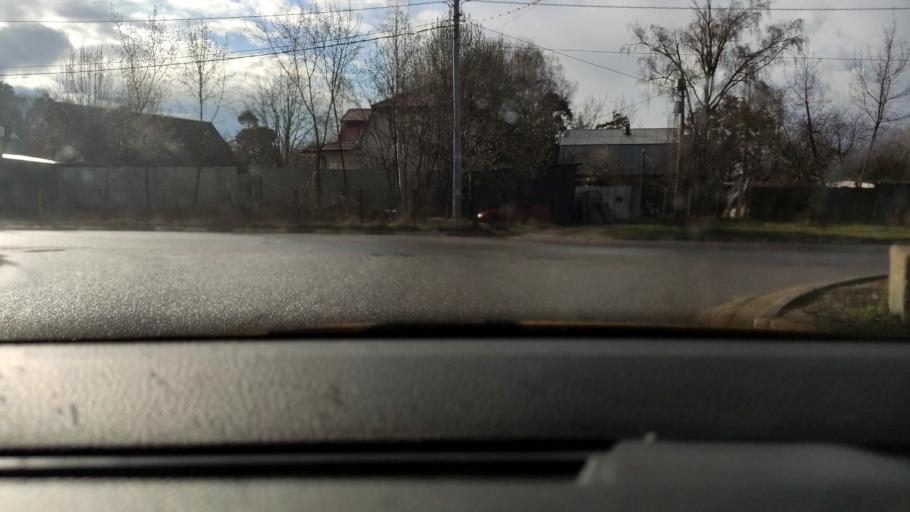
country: RU
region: Moskovskaya
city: Saltykovka
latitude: 55.7454
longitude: 37.9485
